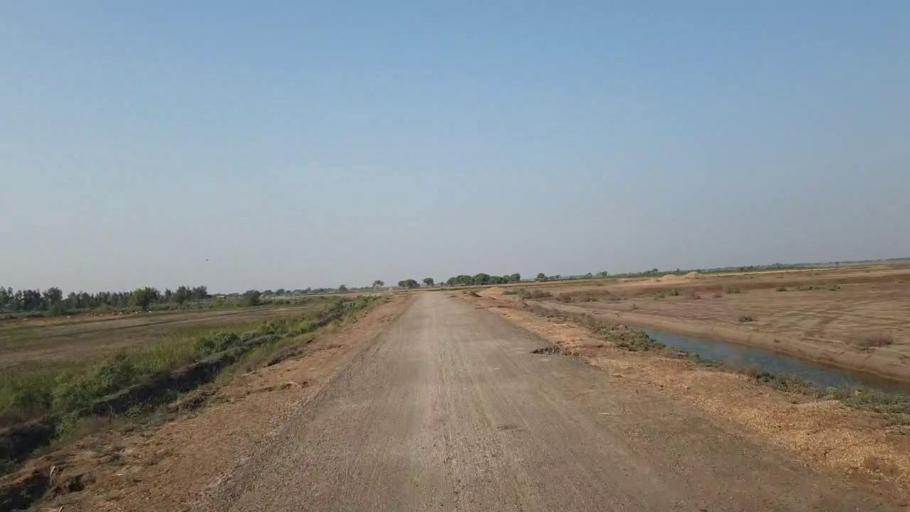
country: PK
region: Sindh
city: Kario
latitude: 24.8986
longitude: 68.6229
